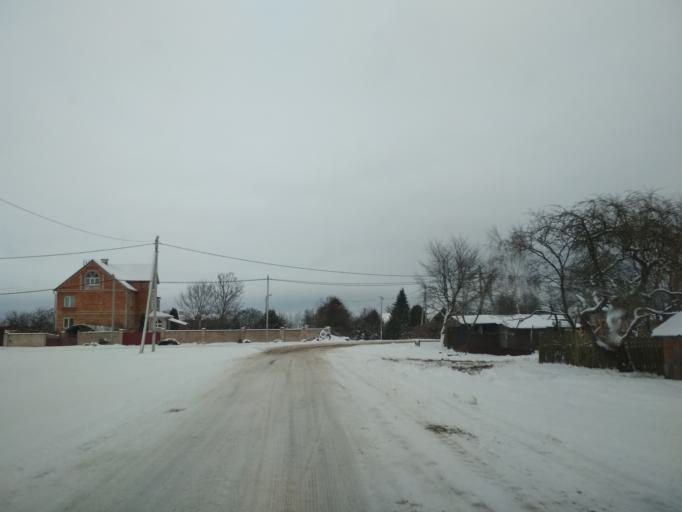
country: BY
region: Minsk
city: Mar''ina Horka
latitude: 53.5357
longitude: 28.1263
